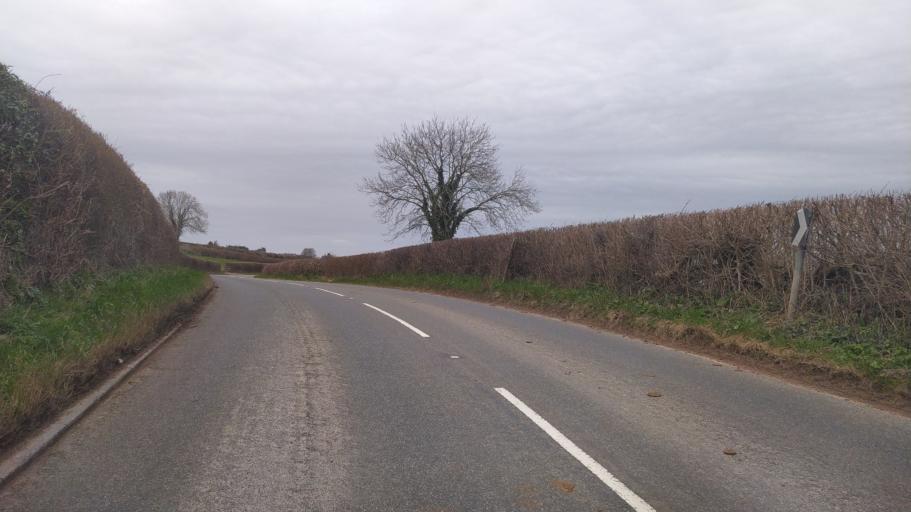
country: GB
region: England
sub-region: Somerset
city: Crewkerne
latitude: 50.8654
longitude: -2.7610
